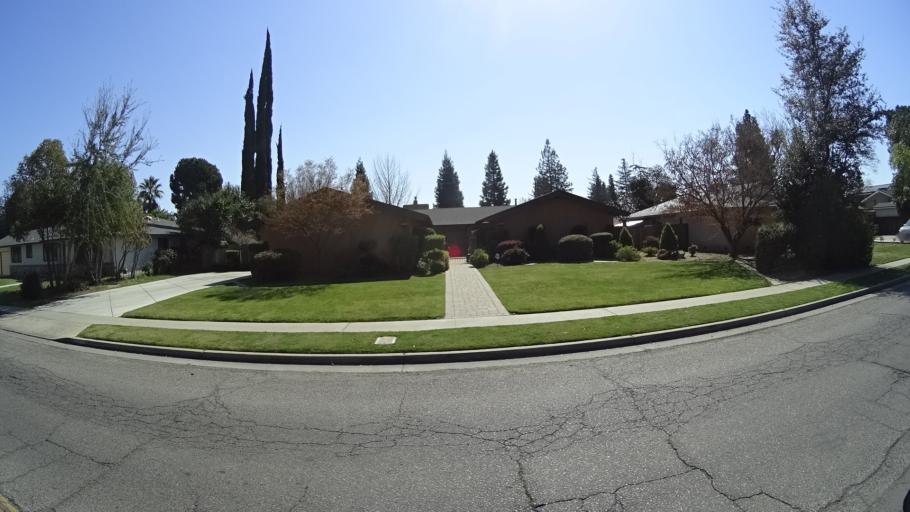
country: US
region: California
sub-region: Fresno County
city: Fresno
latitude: 36.8301
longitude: -119.8134
